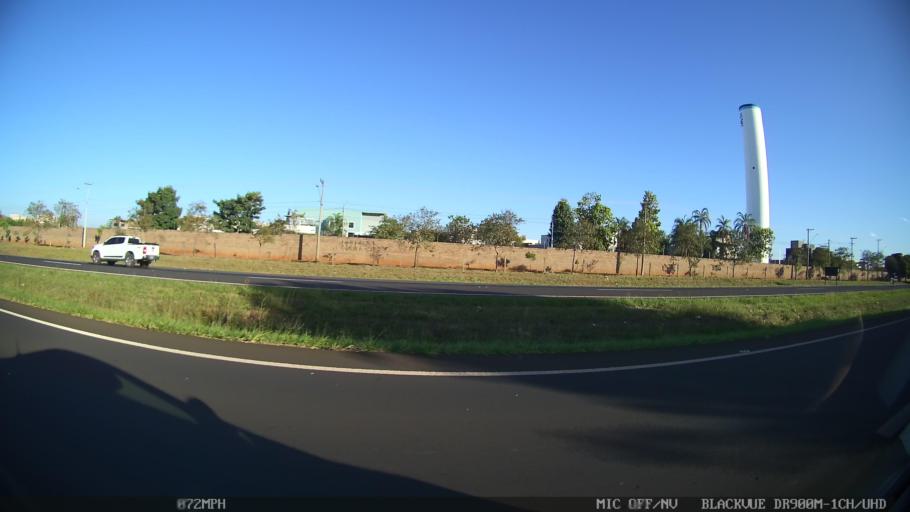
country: BR
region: Sao Paulo
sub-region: Sao Jose Do Rio Preto
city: Sao Jose do Rio Preto
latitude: -20.8005
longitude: -49.3399
